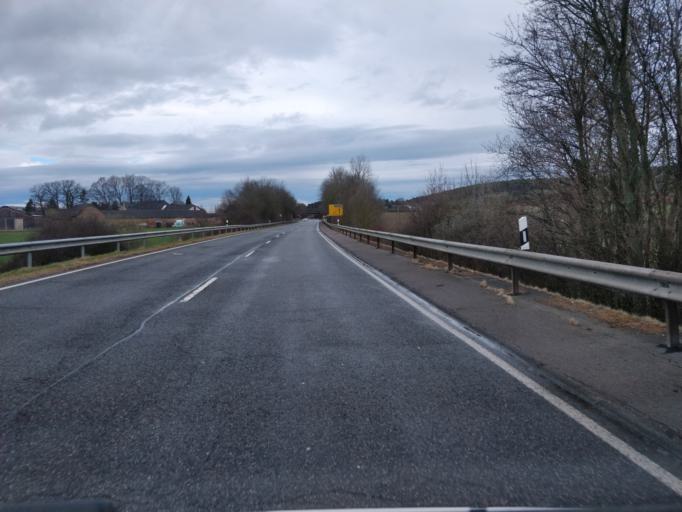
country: DE
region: North Rhine-Westphalia
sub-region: Regierungsbezirk Koln
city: Bad Munstereifel
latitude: 50.5610
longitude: 6.7043
